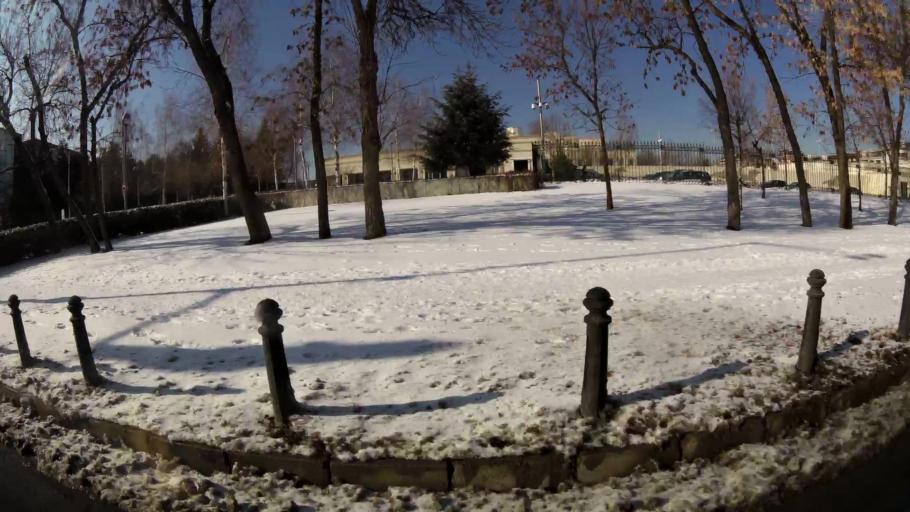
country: BG
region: Sofia-Capital
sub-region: Stolichna Obshtina
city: Sofia
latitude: 42.6666
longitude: 23.3138
